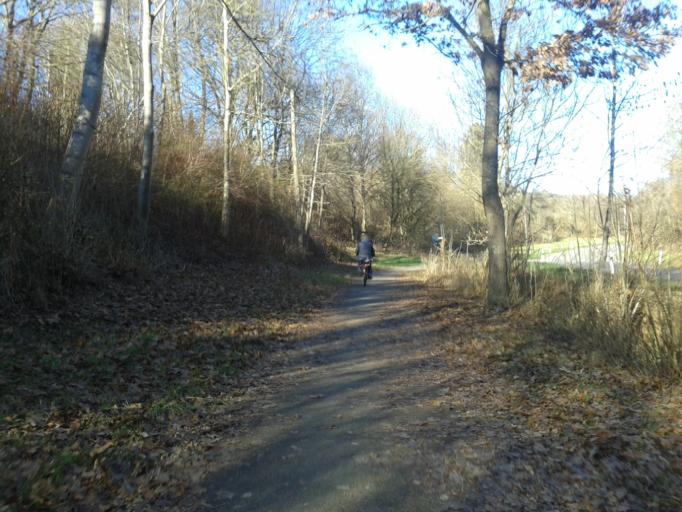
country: DE
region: Baden-Wuerttemberg
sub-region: Tuebingen Region
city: Ulm
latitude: 48.4131
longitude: 9.9690
